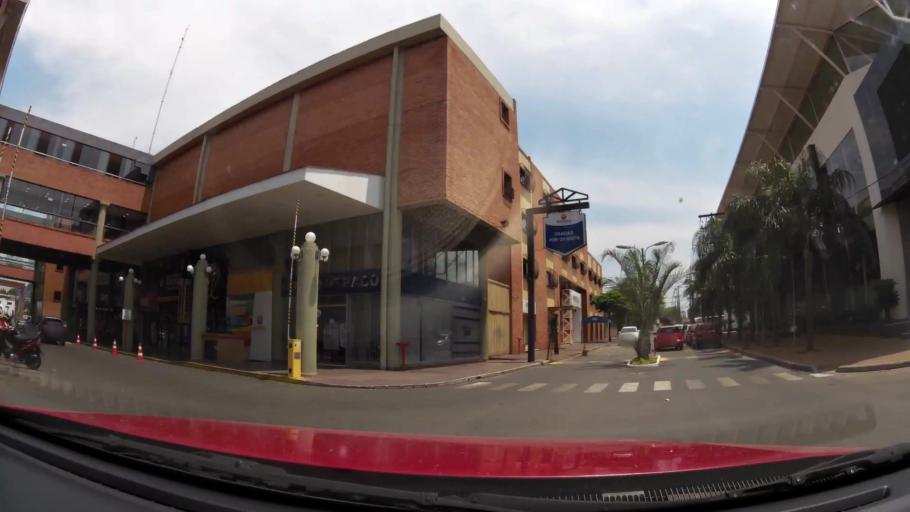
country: PY
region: Central
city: Lambare
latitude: -25.3160
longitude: -57.5714
